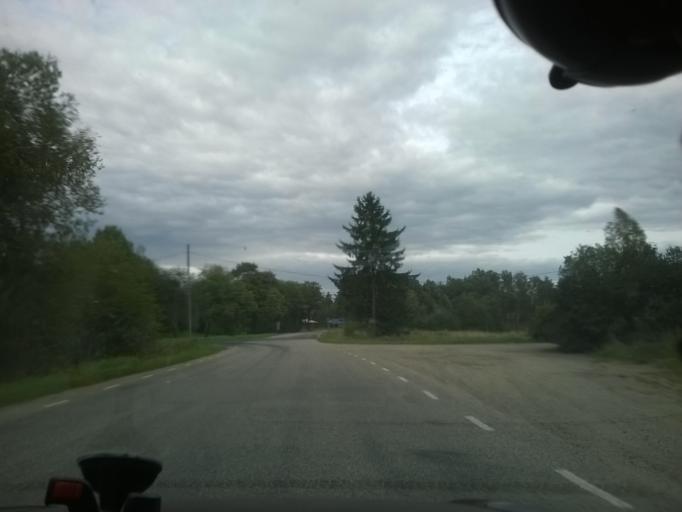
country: EE
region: Vorumaa
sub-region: Voru linn
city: Voru
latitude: 57.7812
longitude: 27.0308
